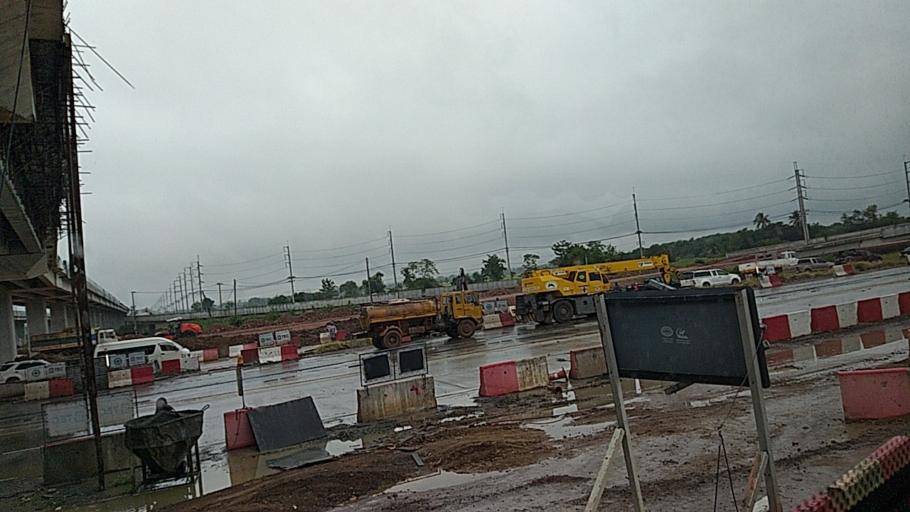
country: TH
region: Nakhon Ratchasima
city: Kham Thale So
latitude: 14.9074
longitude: 101.9205
